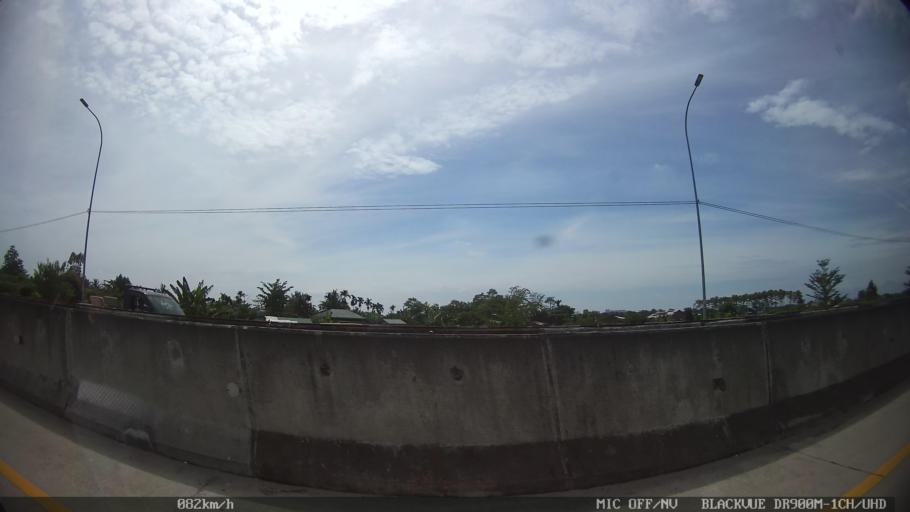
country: ID
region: North Sumatra
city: Medan
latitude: 3.6408
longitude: 98.6458
